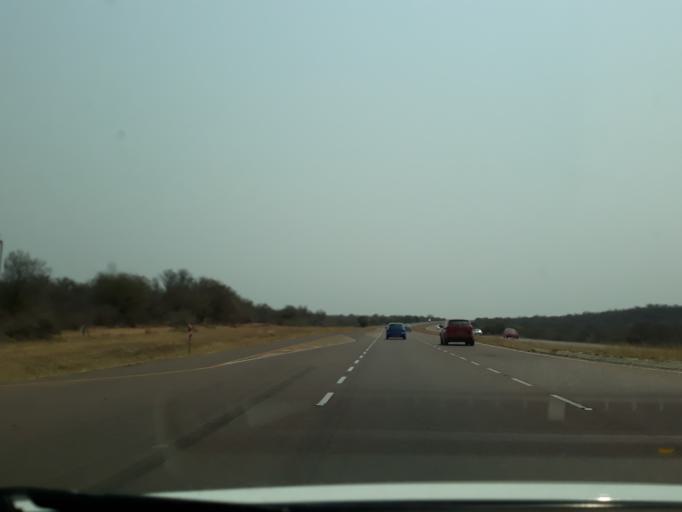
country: BW
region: Kgatleng
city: Bokaa
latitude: -24.4255
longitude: 26.0472
